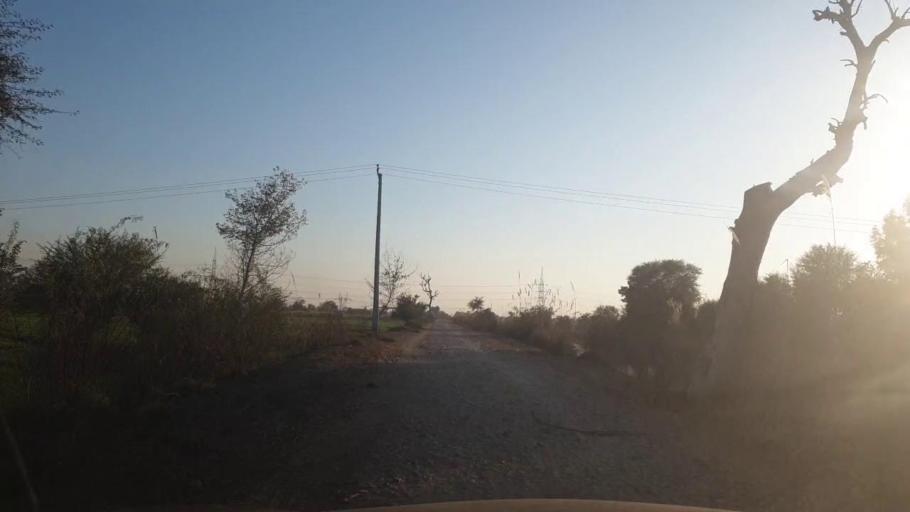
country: PK
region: Sindh
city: Mirpur Mathelo
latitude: 27.9934
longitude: 69.4660
